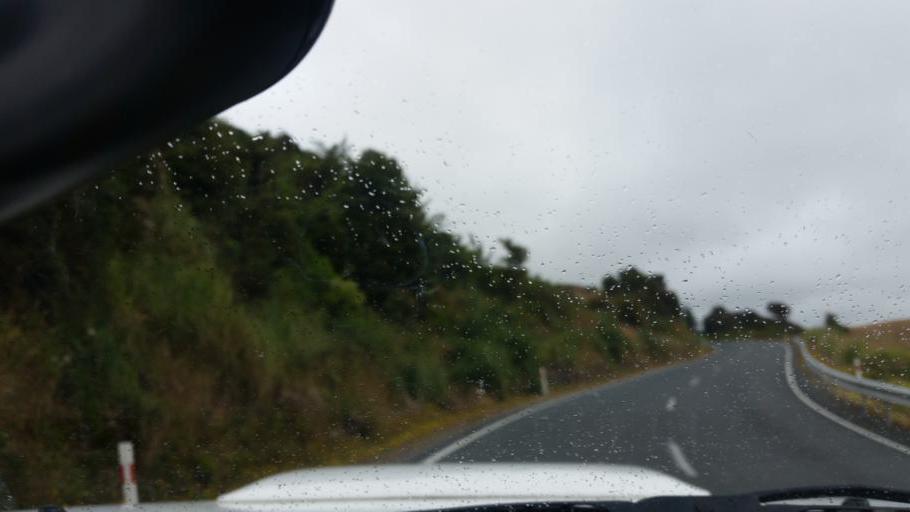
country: NZ
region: Auckland
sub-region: Auckland
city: Wellsford
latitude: -36.1333
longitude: 174.5279
